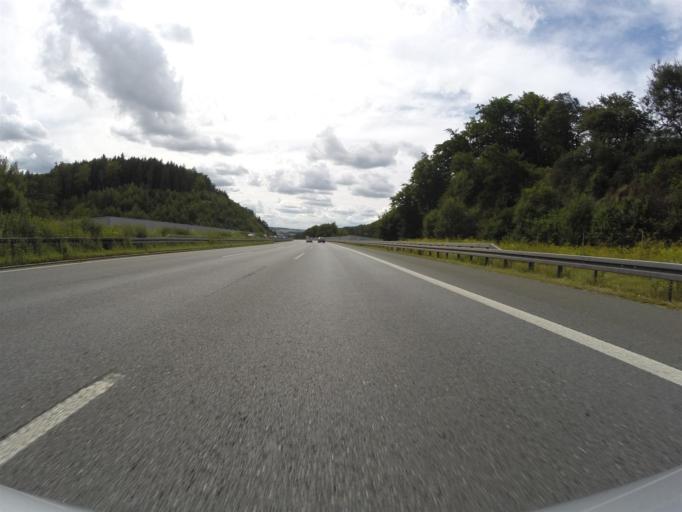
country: DE
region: Bavaria
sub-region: Upper Franconia
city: Marktschorgast
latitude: 50.0757
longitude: 11.6441
